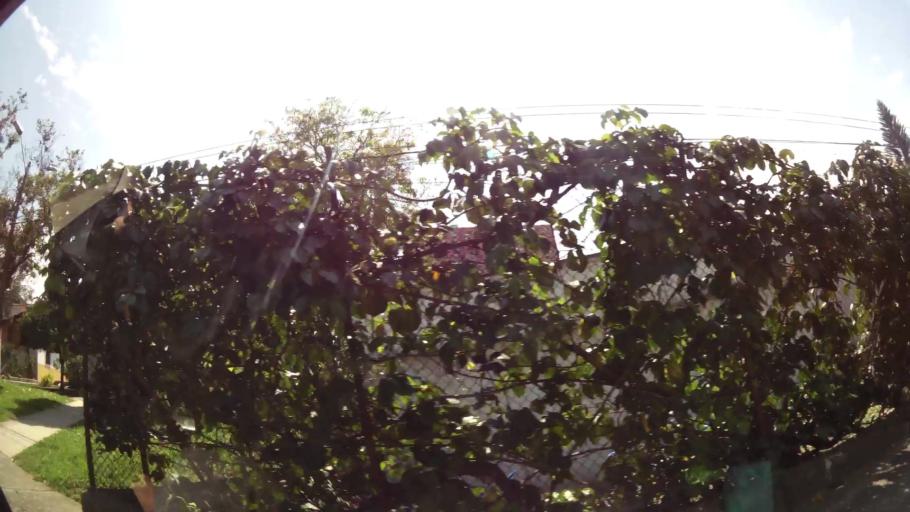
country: CO
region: Antioquia
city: Itagui
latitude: 6.2075
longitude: -75.6005
